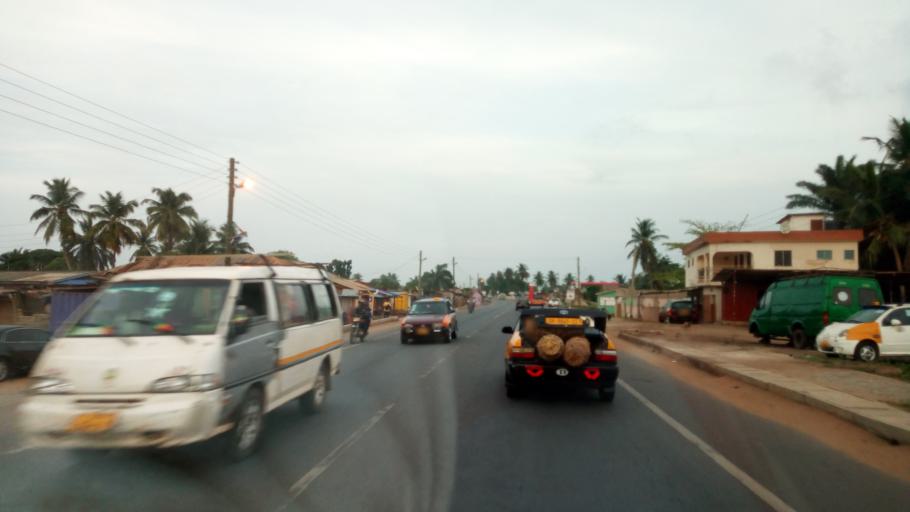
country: TG
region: Maritime
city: Lome
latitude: 6.1184
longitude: 1.1765
